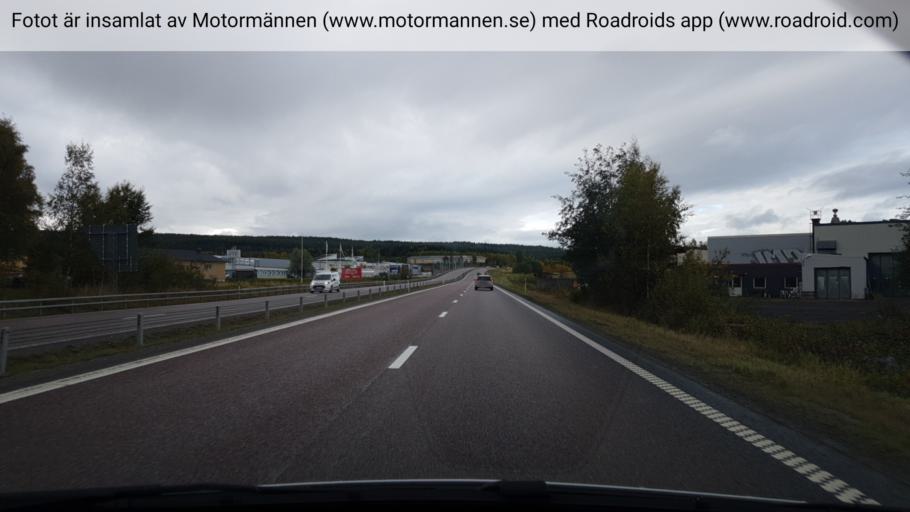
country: SE
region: Vaesternorrland
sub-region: OErnskoeldsviks Kommun
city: Ornskoldsvik
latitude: 63.3114
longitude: 18.7862
